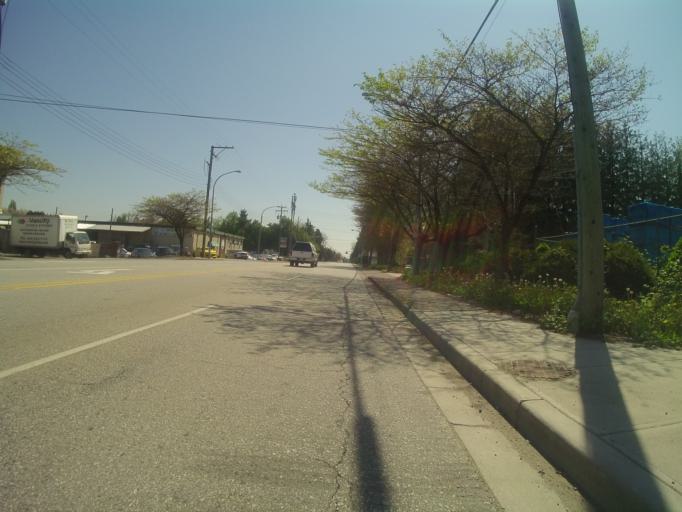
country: CA
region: British Columbia
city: Richmond
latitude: 49.1915
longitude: -123.0916
